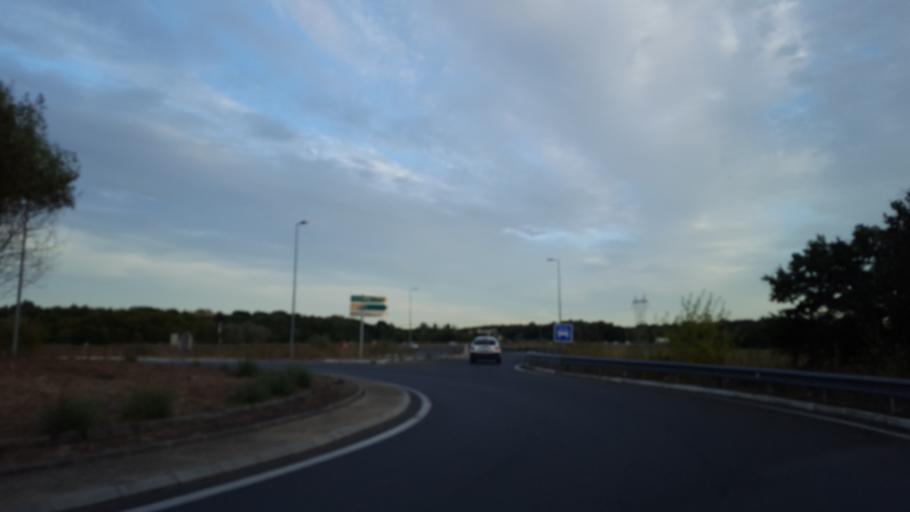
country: FR
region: Pays de la Loire
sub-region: Departement de la Loire-Atlantique
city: Basse-Goulaine
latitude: 47.2173
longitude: -1.4565
